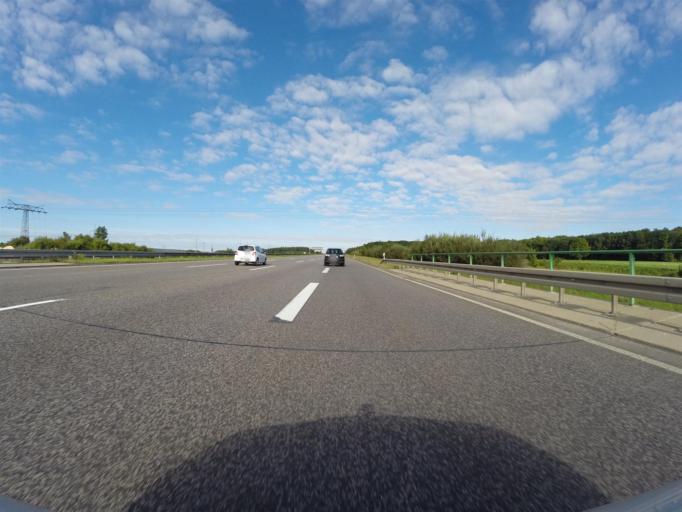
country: DE
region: Thuringia
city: Hetschburg
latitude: 50.9450
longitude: 11.2928
